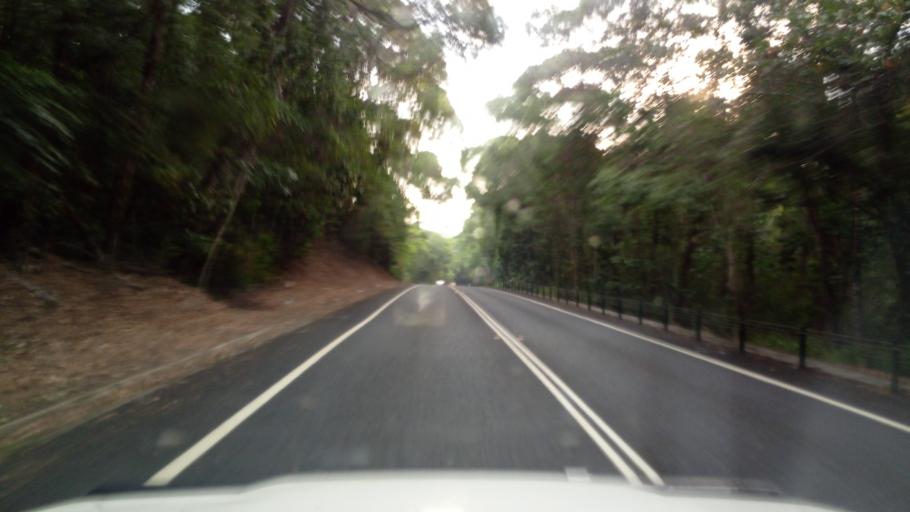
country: AU
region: Queensland
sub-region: Tablelands
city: Kuranda
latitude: -16.8435
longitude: 145.6092
